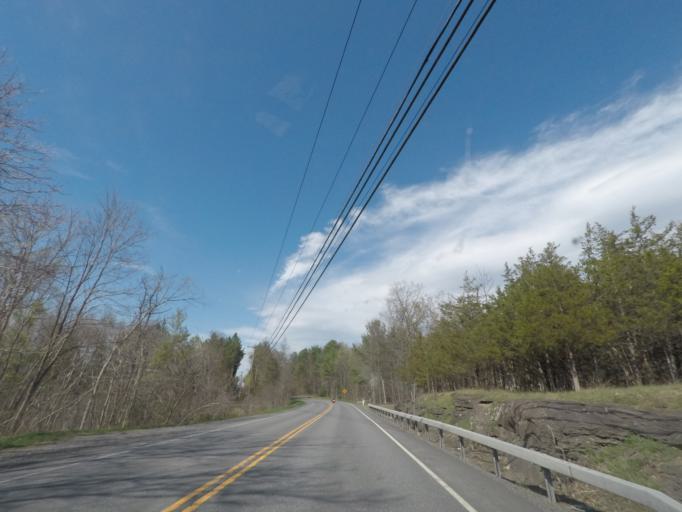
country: US
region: New York
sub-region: Greene County
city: Cairo
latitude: 42.3884
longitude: -74.0302
